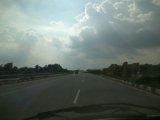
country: IN
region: Karnataka
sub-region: Kolar
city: Kolar
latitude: 13.1353
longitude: 78.0152
